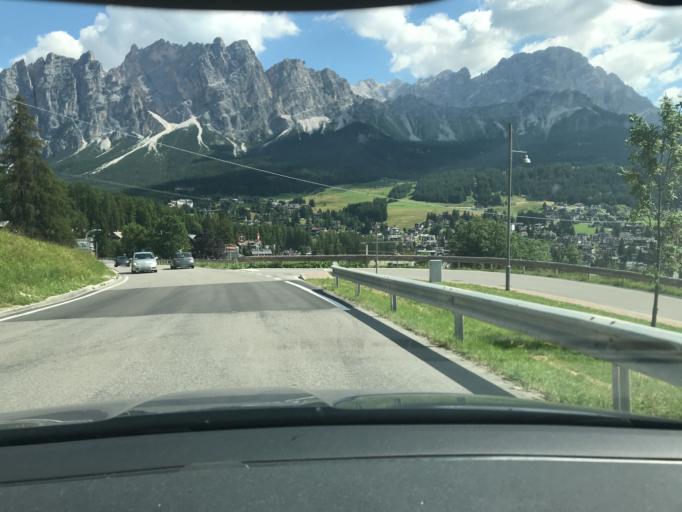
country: IT
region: Veneto
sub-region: Provincia di Belluno
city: Cortina d'Ampezzo
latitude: 46.5397
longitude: 12.1243
